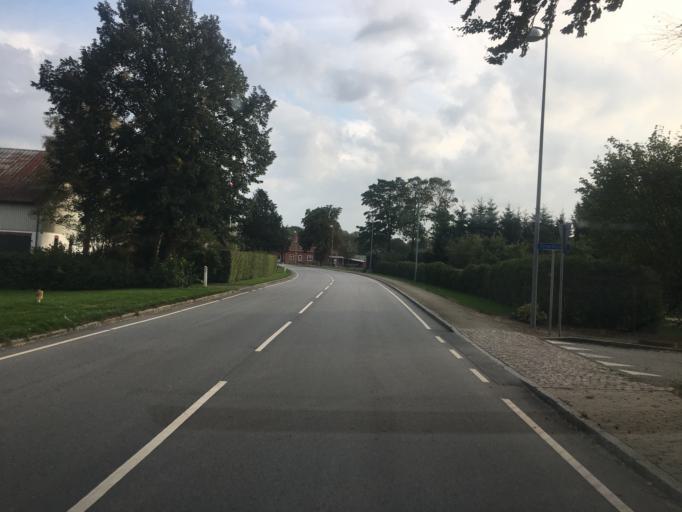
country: DE
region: Schleswig-Holstein
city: Bramstedtlund
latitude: 54.9171
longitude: 9.0709
